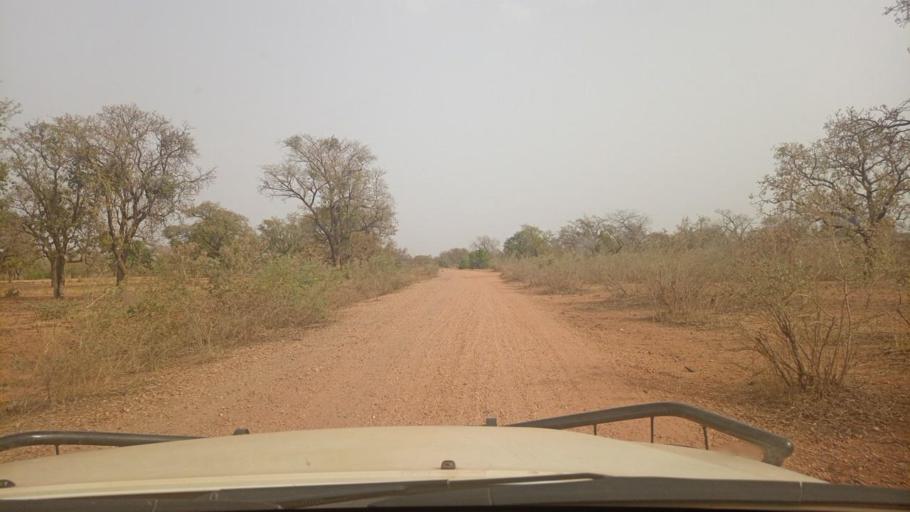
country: BF
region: Boucle du Mouhoun
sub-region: Province des Banwa
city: Salanso
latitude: 12.0969
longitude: -4.3319
